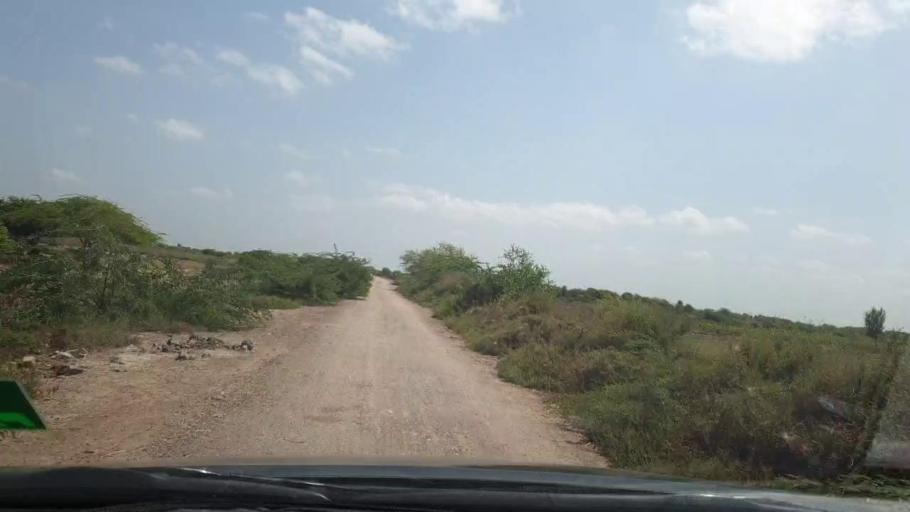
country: PK
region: Sindh
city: Tando Bago
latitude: 24.8613
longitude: 69.0997
